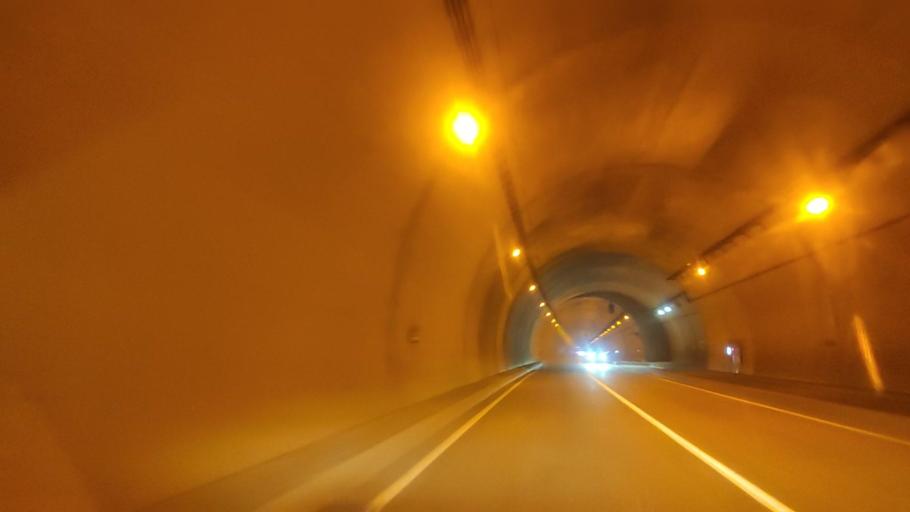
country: JP
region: Hokkaido
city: Date
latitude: 42.5629
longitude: 140.7838
